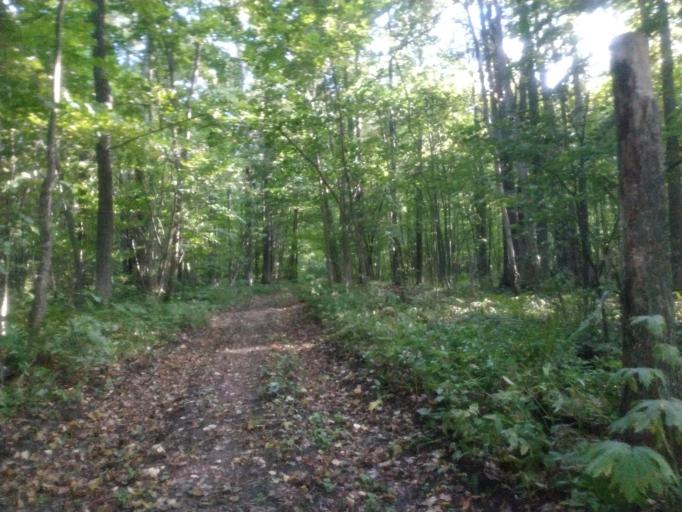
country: RU
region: Chuvashia
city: Novyye Lapsary
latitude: 56.1370
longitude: 47.1097
